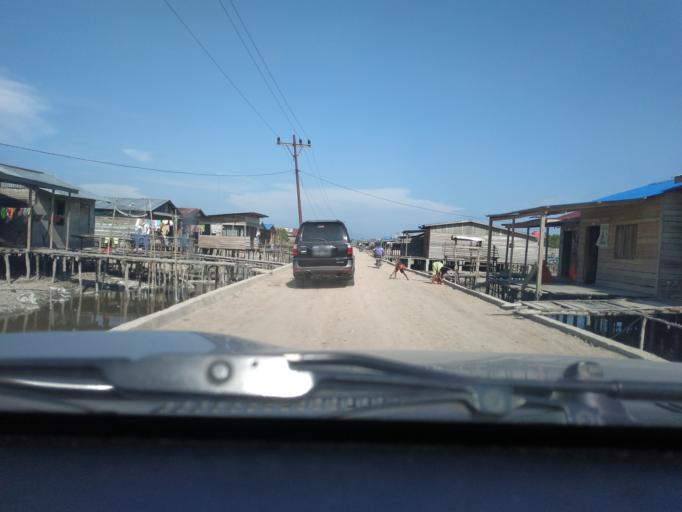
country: ID
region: North Sumatra
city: Tanjungbalai
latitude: 2.8191
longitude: 99.9888
